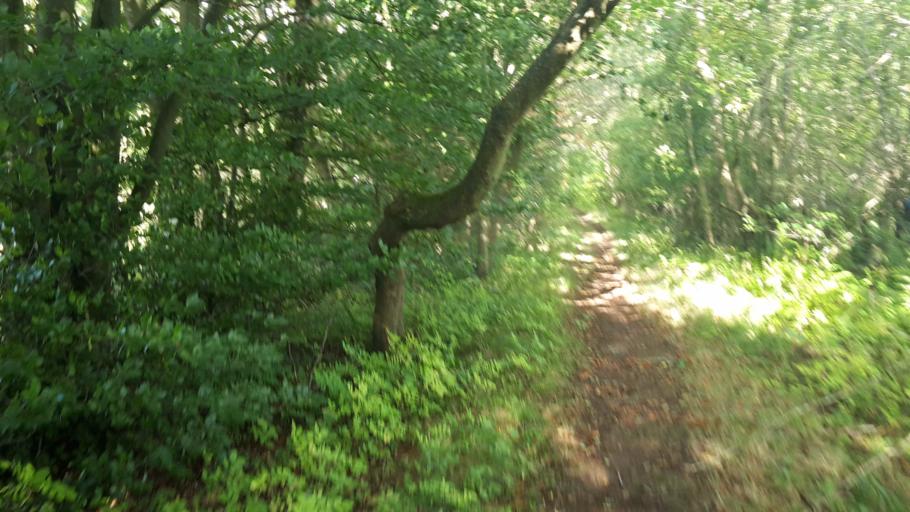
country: GB
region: Scotland
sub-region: South Lanarkshire
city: Law
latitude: 55.7275
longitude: -3.8660
